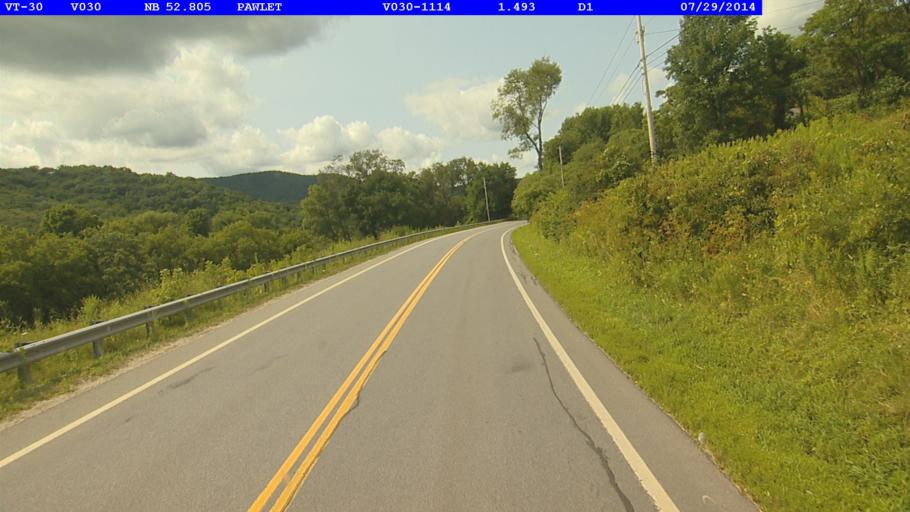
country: US
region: New York
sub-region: Washington County
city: Granville
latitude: 43.3317
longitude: -73.1752
